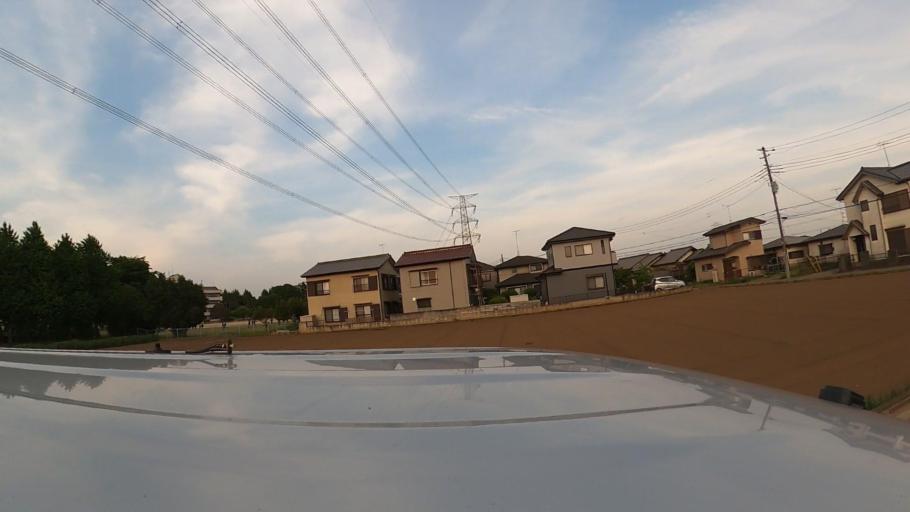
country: JP
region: Ibaraki
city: Ushiku
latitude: 36.0044
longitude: 140.1227
